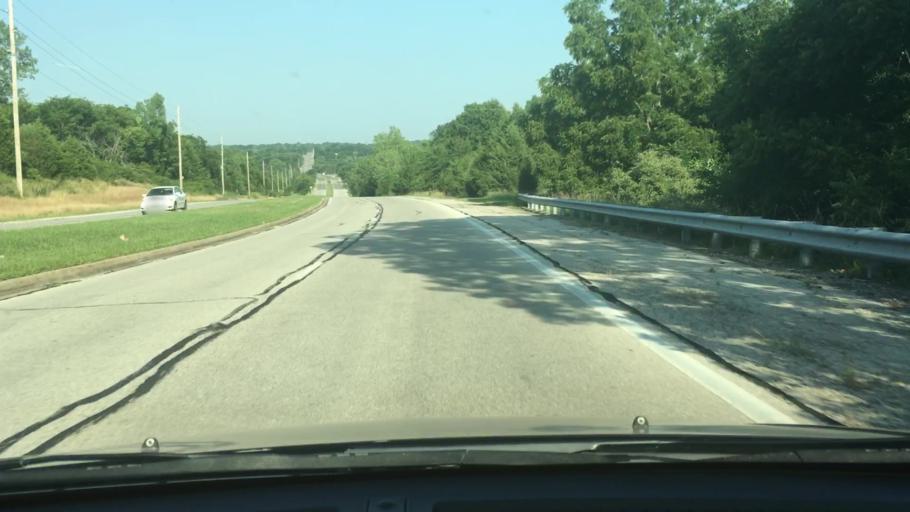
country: US
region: Missouri
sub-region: Jackson County
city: Grandview
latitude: 38.8852
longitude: -94.4809
